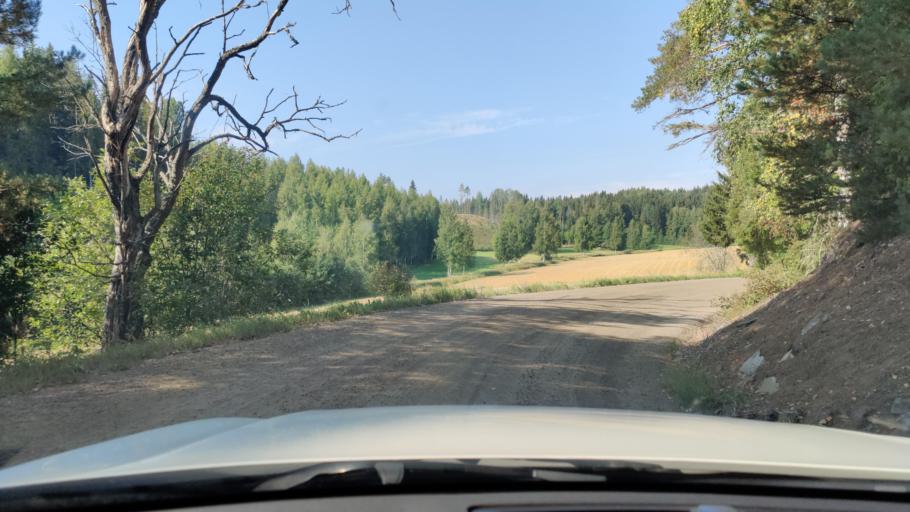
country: FI
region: Haeme
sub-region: Haemeenlinna
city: Tervakoski
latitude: 60.6740
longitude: 24.6055
